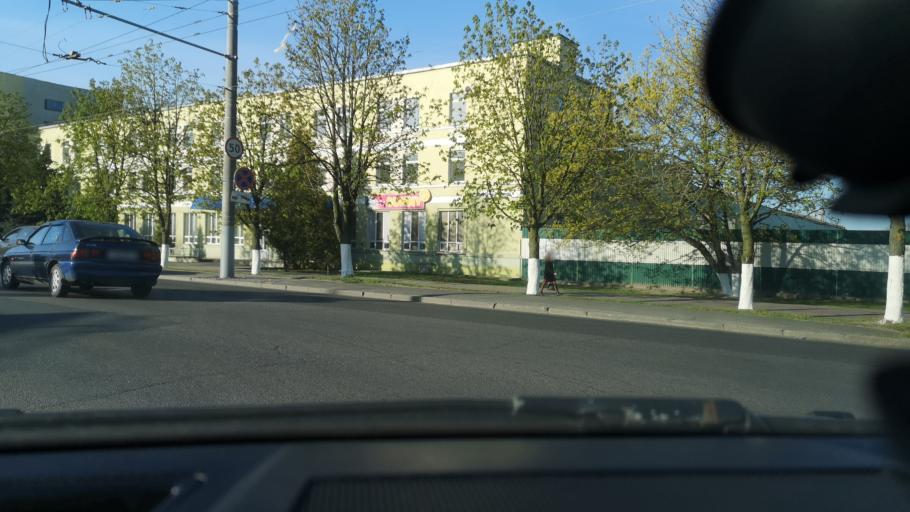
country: BY
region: Gomel
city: Gomel
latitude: 52.4500
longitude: 30.9964
